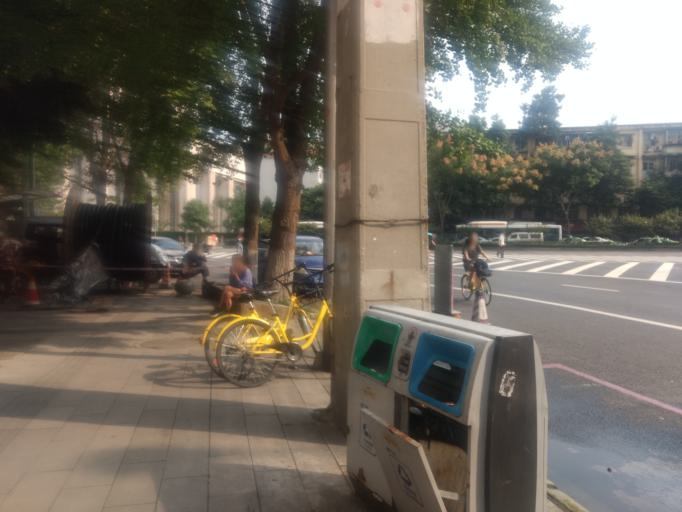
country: CN
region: Sichuan
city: Chengdu
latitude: 30.6731
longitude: 104.0682
